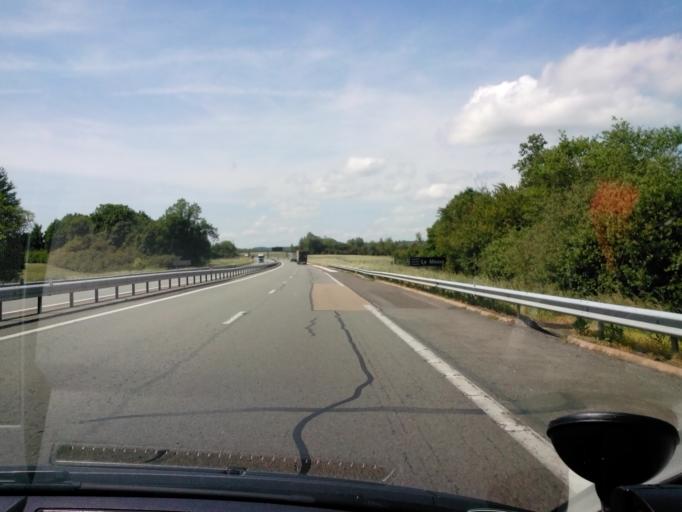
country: FR
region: Champagne-Ardenne
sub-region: Departement de la Haute-Marne
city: Avrecourt
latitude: 48.0202
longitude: 5.5302
